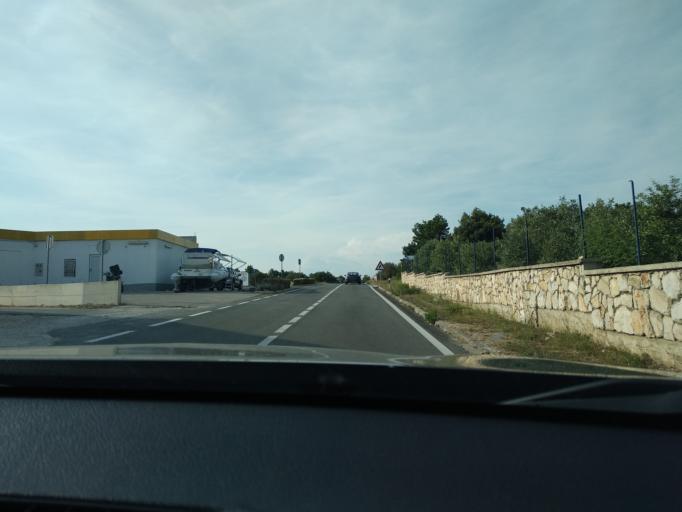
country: HR
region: Sibensko-Kniniska
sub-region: Grad Sibenik
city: Tisno
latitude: 43.7923
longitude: 15.6328
